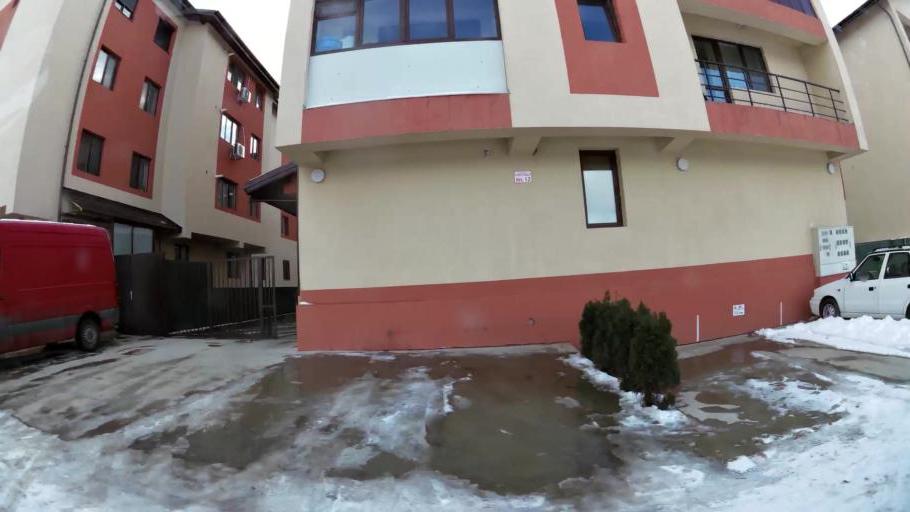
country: RO
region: Ilfov
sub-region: Comuna Fundeni-Dobroesti
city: Fundeni
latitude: 44.4635
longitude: 26.1666
